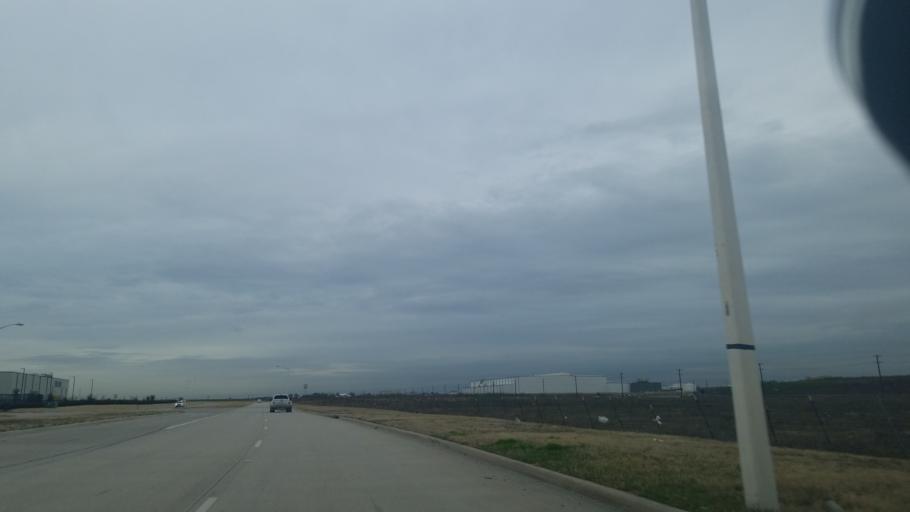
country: US
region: Texas
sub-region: Denton County
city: Denton
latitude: 33.2096
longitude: -97.1844
